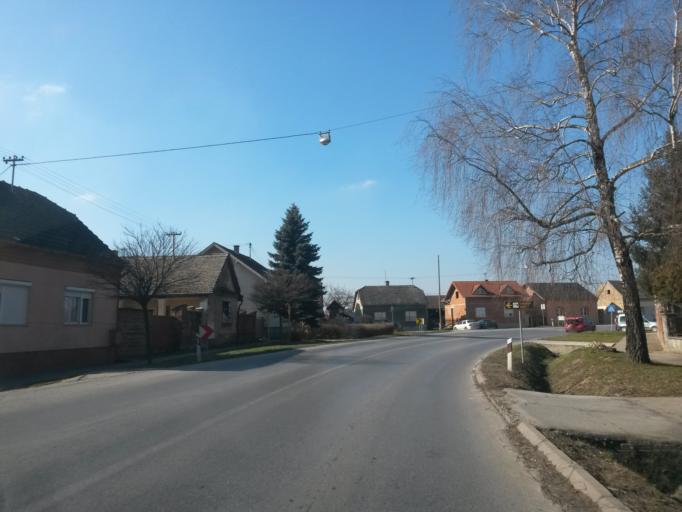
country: HR
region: Osjecko-Baranjska
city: Petrijevci
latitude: 45.6141
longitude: 18.5375
